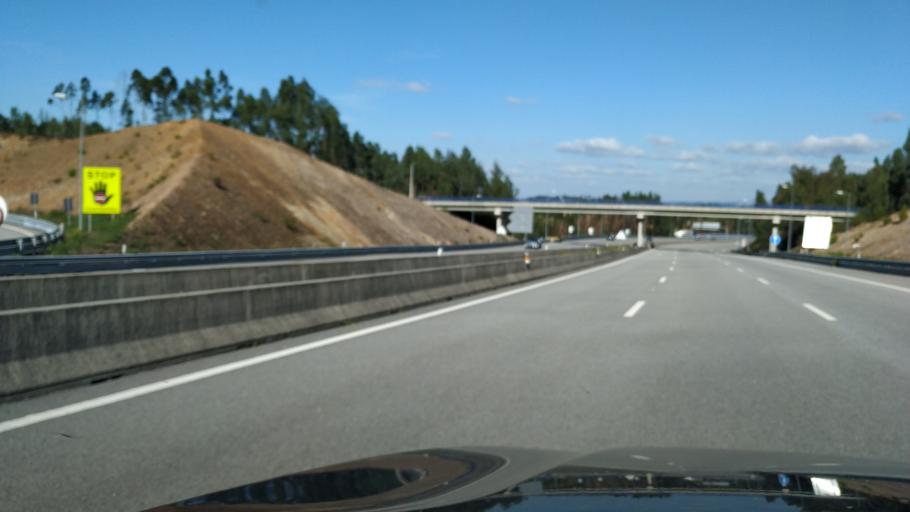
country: PT
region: Aveiro
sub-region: Santa Maria da Feira
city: Lobao
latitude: 41.0156
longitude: -8.4778
